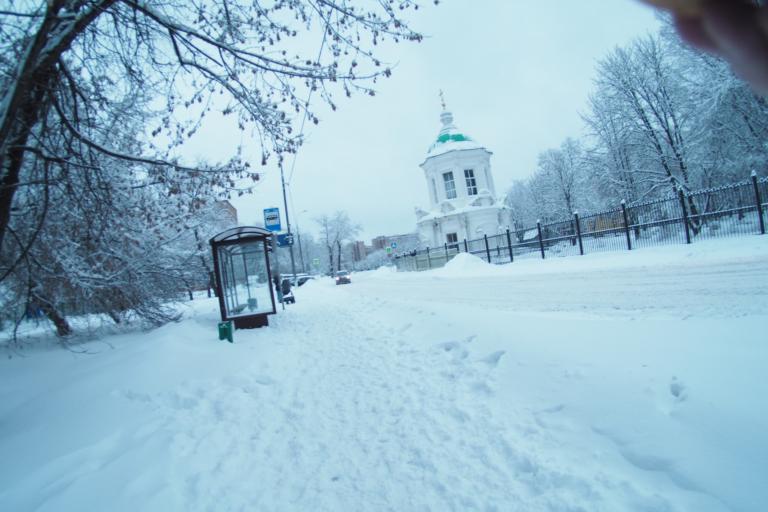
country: RU
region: Moscow
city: Ryazanskiy
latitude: 55.7429
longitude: 37.7725
